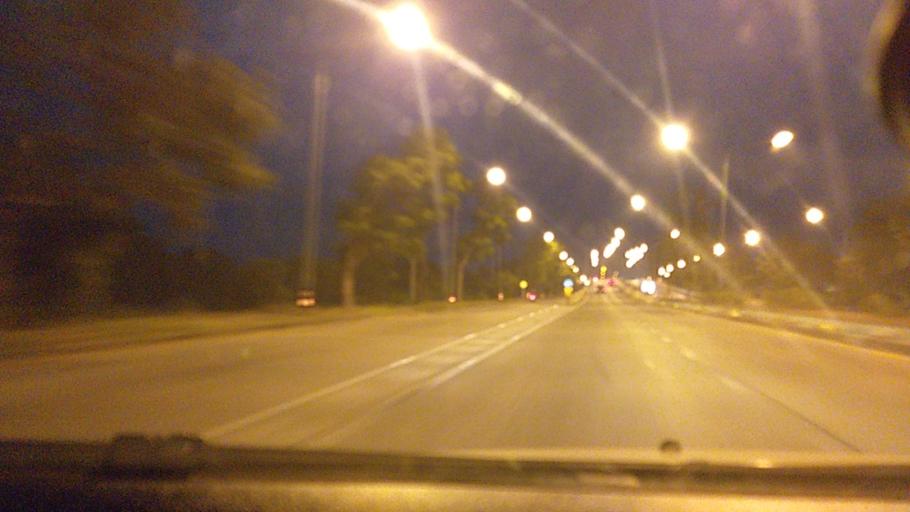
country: TH
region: Sing Buri
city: Sing Buri
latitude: 14.8708
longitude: 100.4173
